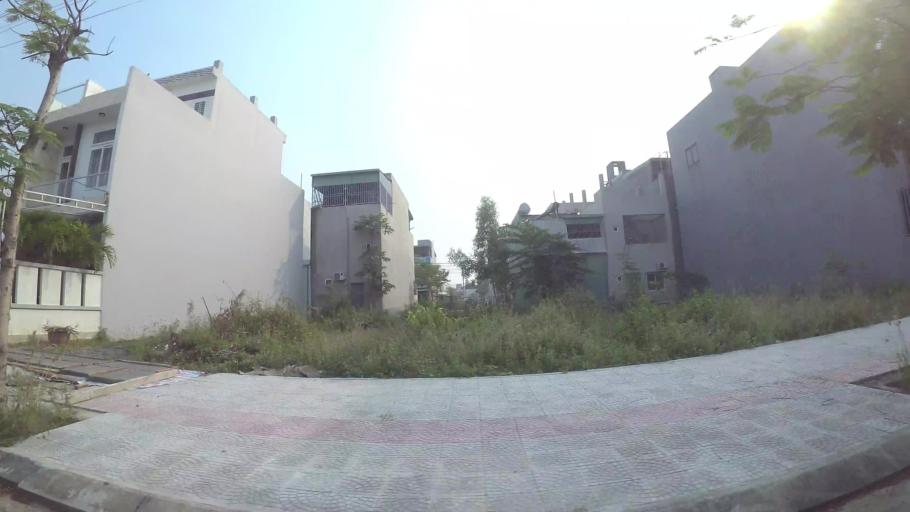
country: VN
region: Da Nang
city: Cam Le
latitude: 16.0101
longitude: 108.2193
